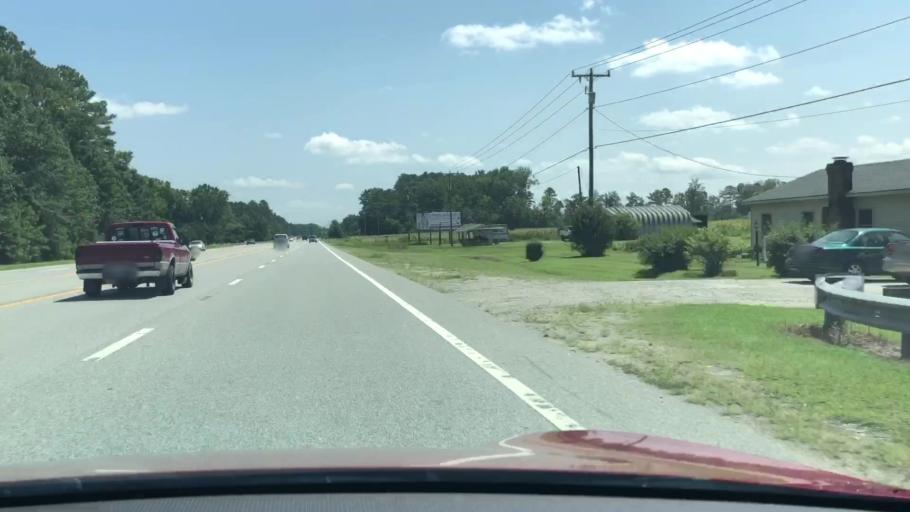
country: US
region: North Carolina
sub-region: Currituck County
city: Moyock
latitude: 36.4734
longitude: -76.1190
